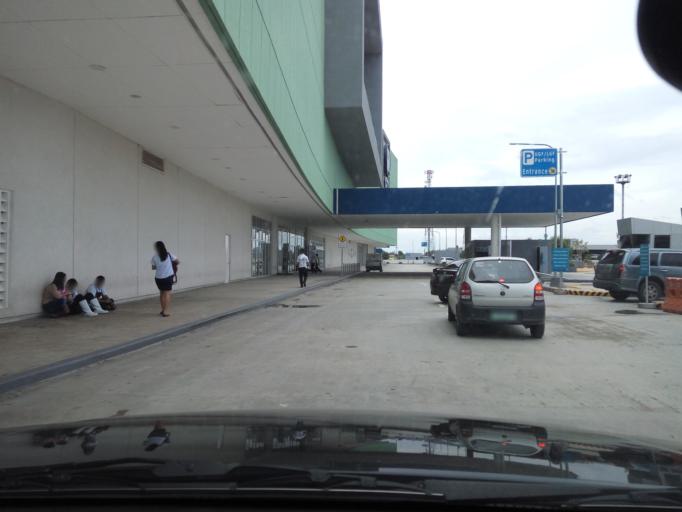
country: PH
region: Central Luzon
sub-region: Province of Nueva Ecija
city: Cabanatuan City
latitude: 15.4660
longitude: 120.9552
